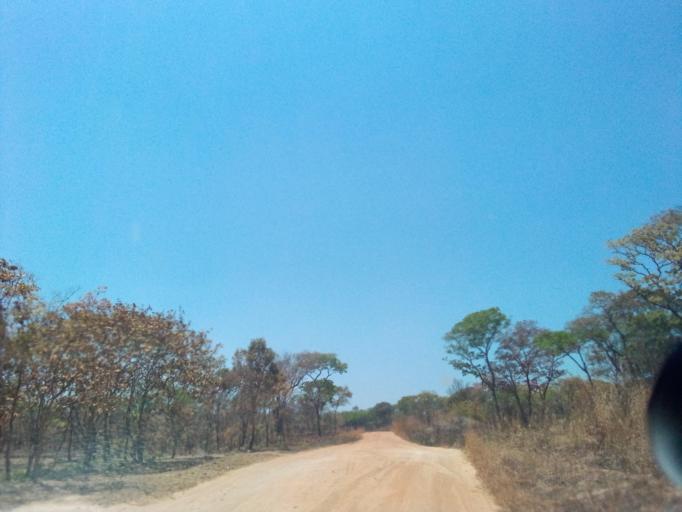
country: ZM
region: Northern
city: Mpika
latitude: -12.2543
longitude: 30.6856
